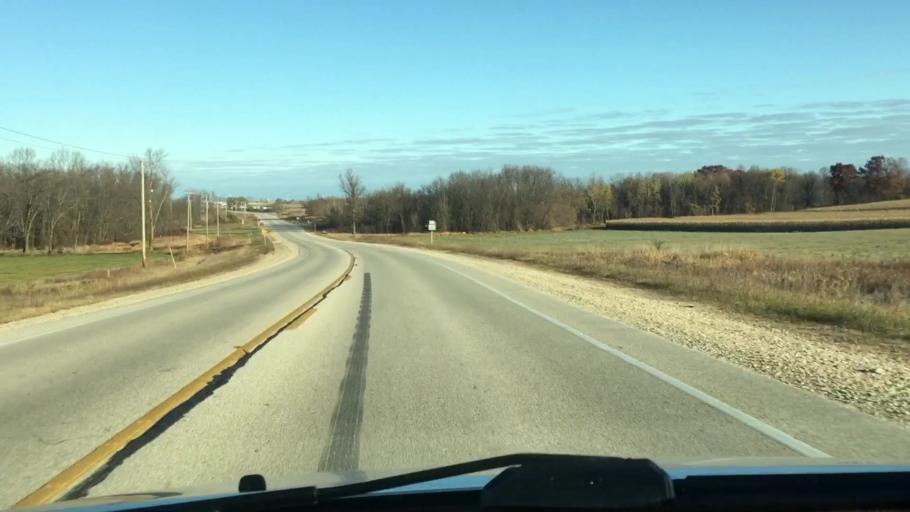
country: US
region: Wisconsin
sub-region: Dodge County
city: Lomira
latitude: 43.5549
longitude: -88.4438
